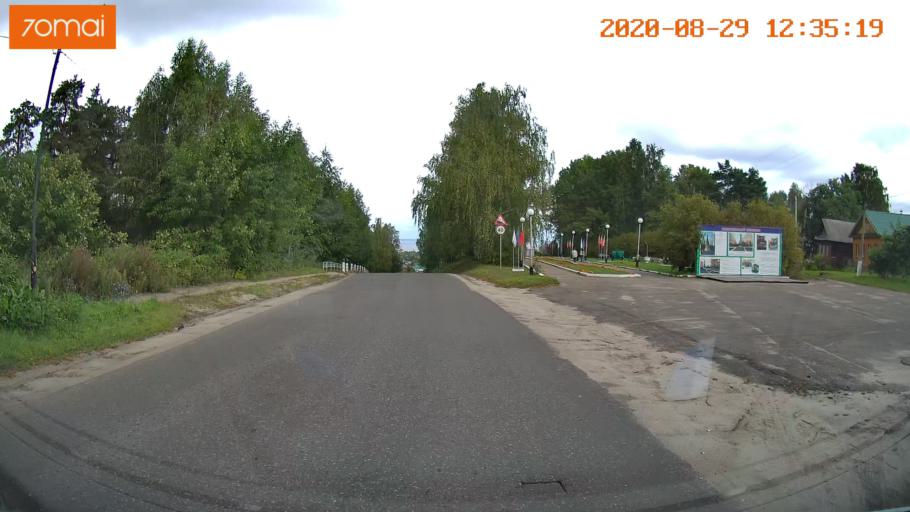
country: RU
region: Ivanovo
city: Yur'yevets
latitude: 57.3130
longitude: 43.1067
